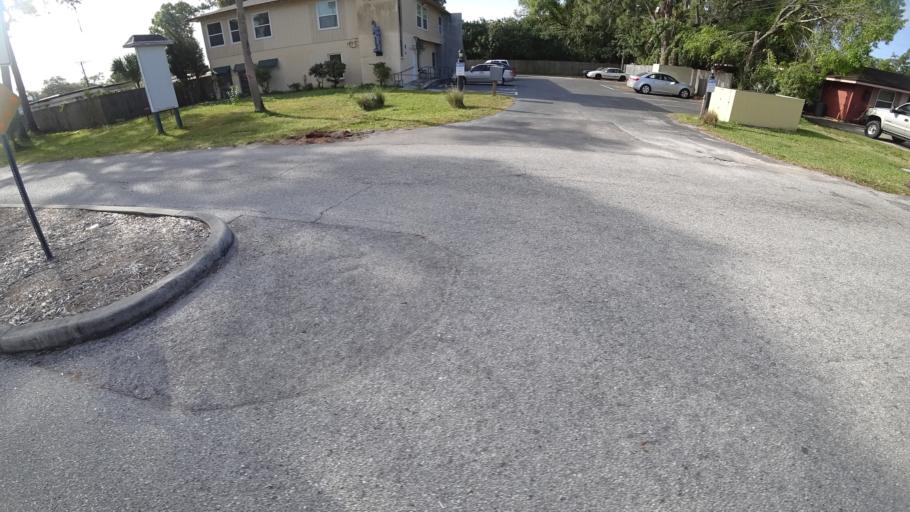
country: US
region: Florida
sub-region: Manatee County
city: Whitfield
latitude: 27.4230
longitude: -82.5477
